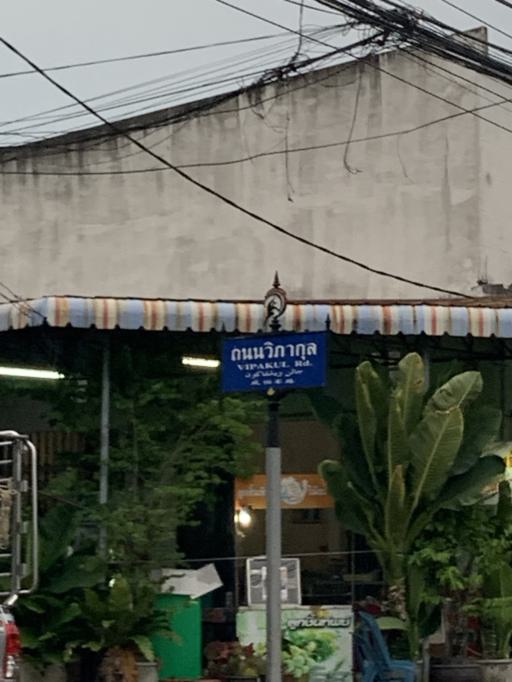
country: TH
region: Yala
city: Yala
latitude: 6.5517
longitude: 101.2871
